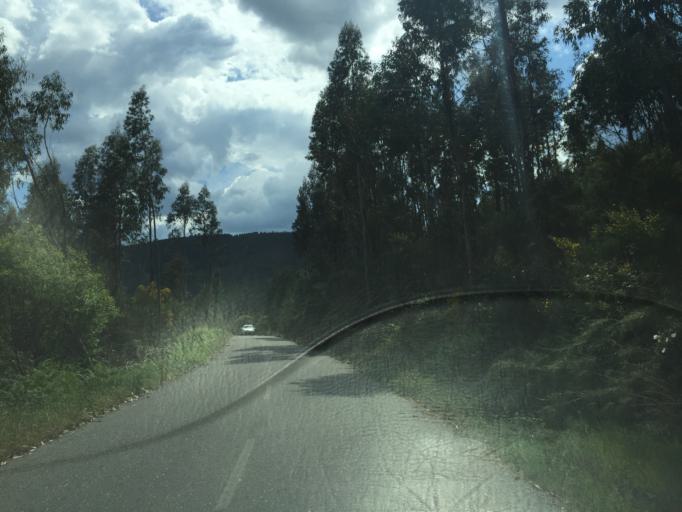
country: PT
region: Coimbra
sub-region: Pampilhosa da Serra
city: Pampilhosa da Serra
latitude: 40.0557
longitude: -7.8084
